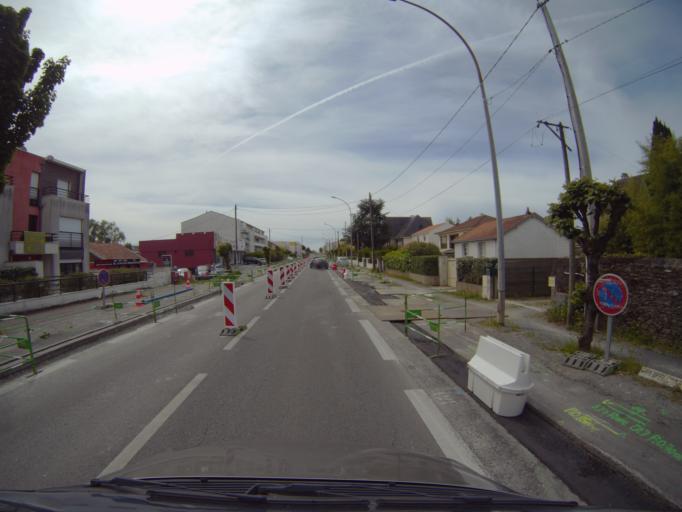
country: FR
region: Pays de la Loire
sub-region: Departement de la Loire-Atlantique
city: Reze
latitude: 47.1709
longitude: -1.5433
